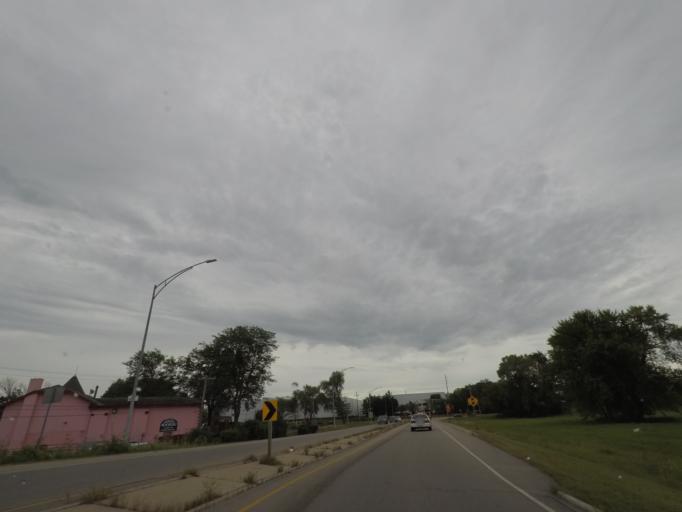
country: US
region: Wisconsin
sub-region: Dane County
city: Monona
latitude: 43.0857
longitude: -89.3101
